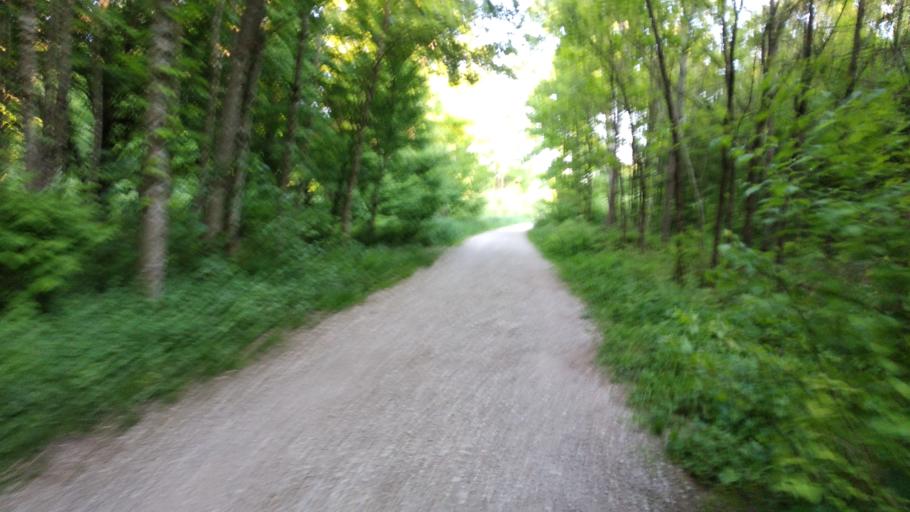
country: DE
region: Bavaria
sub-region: Upper Bavaria
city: Zorneding
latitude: 48.0933
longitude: 11.8018
